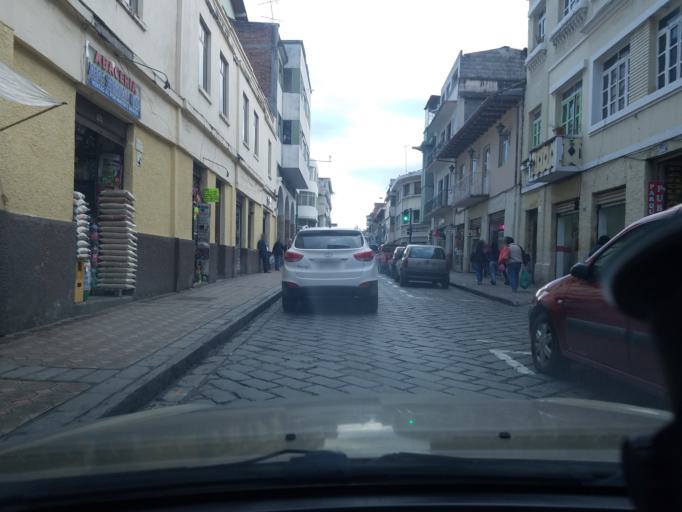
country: EC
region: Azuay
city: Cuenca
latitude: -2.8950
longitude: -79.0015
